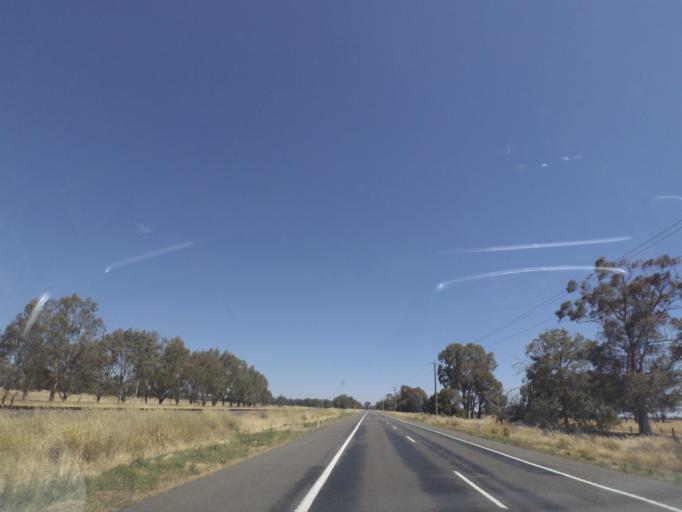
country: AU
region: Victoria
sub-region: Greater Shepparton
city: Shepparton
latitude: -36.2185
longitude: 145.4318
